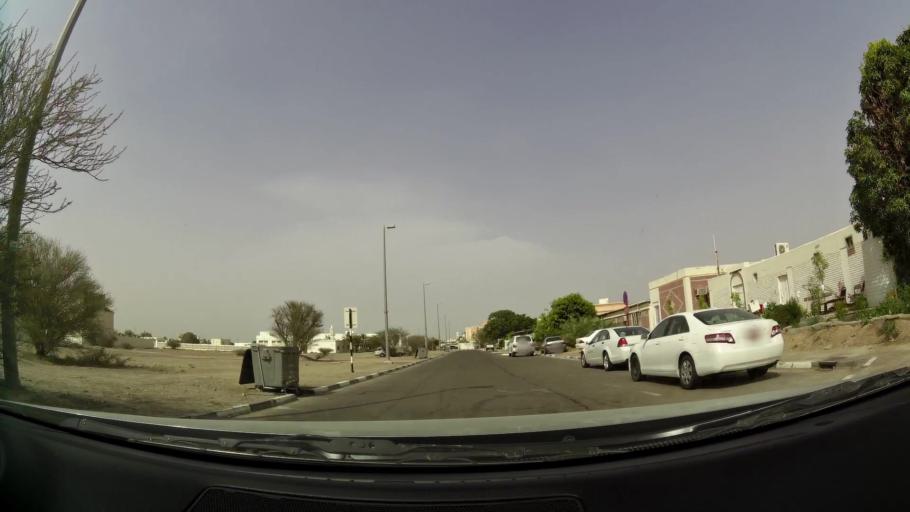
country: AE
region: Abu Dhabi
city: Al Ain
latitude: 24.1805
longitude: 55.6101
